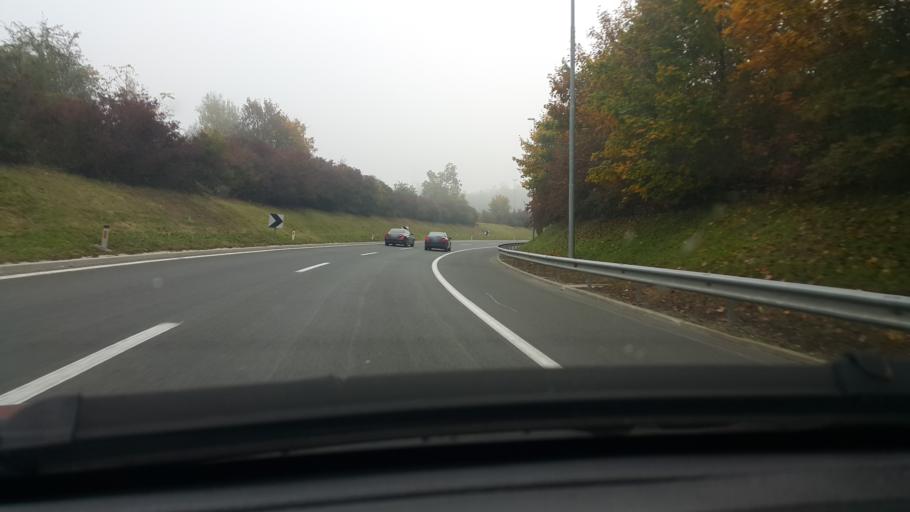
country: SI
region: Dol pri Ljubljani
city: Dol pri Ljubljani
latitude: 46.0672
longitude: 14.5743
